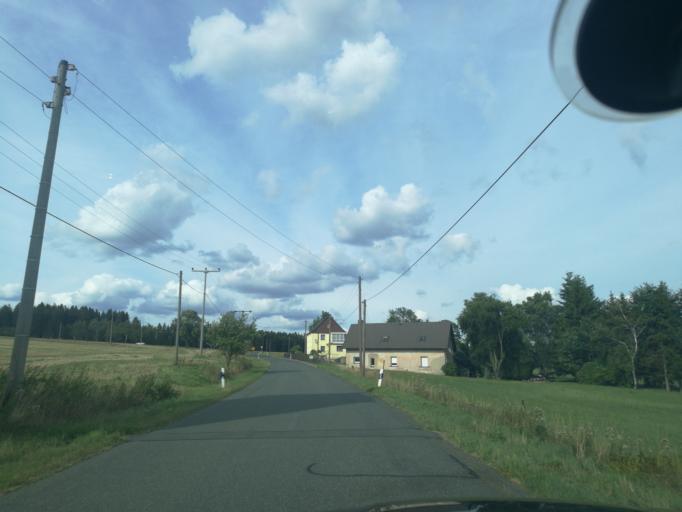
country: DE
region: Saxony
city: Triebel
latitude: 50.3306
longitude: 12.1194
